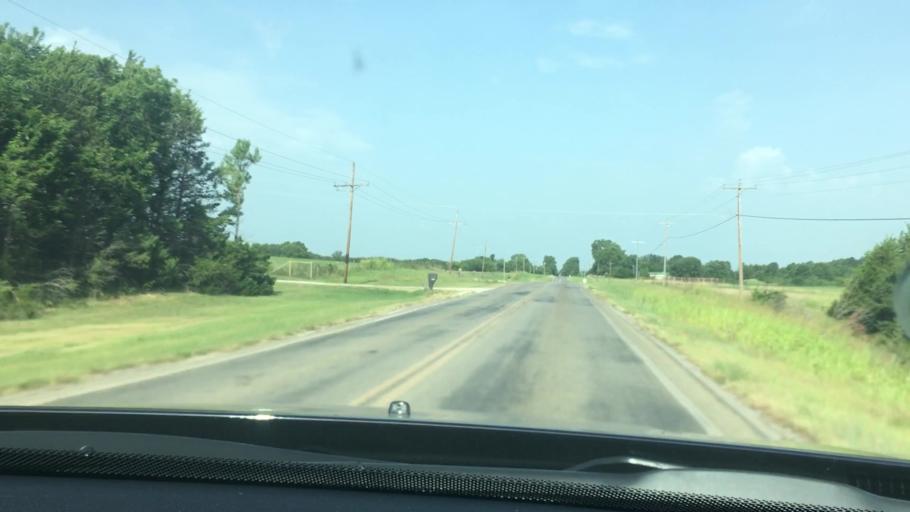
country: US
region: Oklahoma
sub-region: Pontotoc County
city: Byng
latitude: 34.8685
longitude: -96.6502
